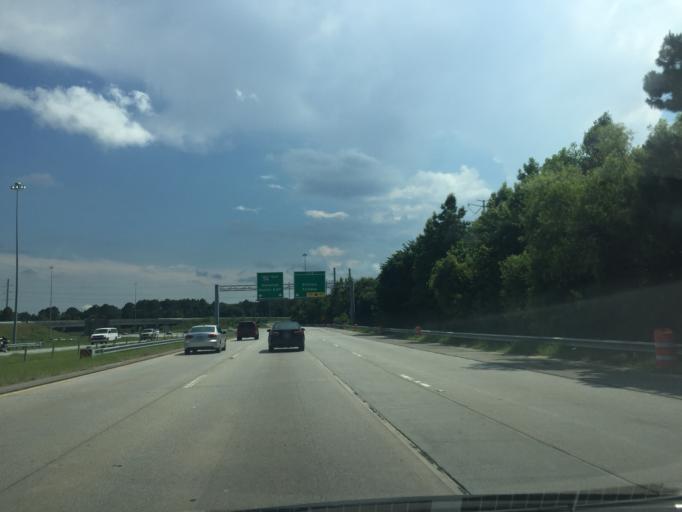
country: US
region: Georgia
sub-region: Chatham County
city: Savannah
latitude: 32.0457
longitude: -81.1459
